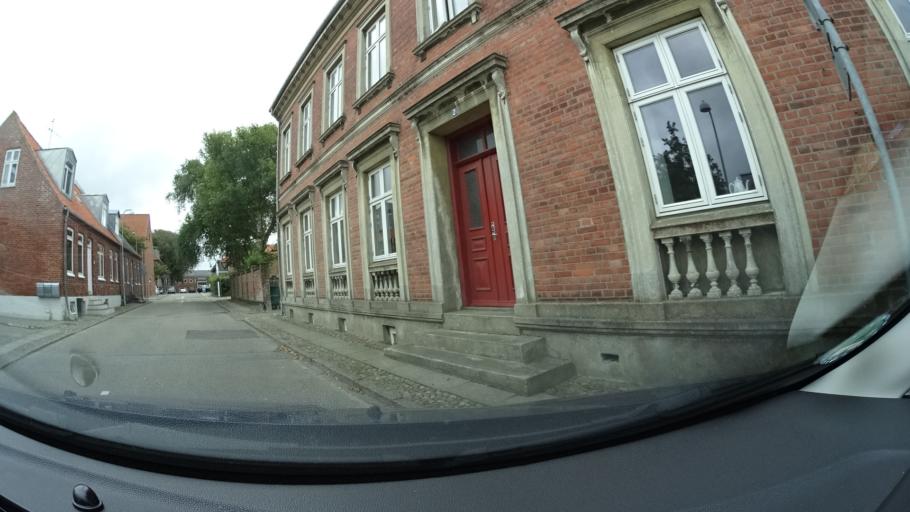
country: DK
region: Central Jutland
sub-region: Ringkobing-Skjern Kommune
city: Ringkobing
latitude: 56.0914
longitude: 8.2488
